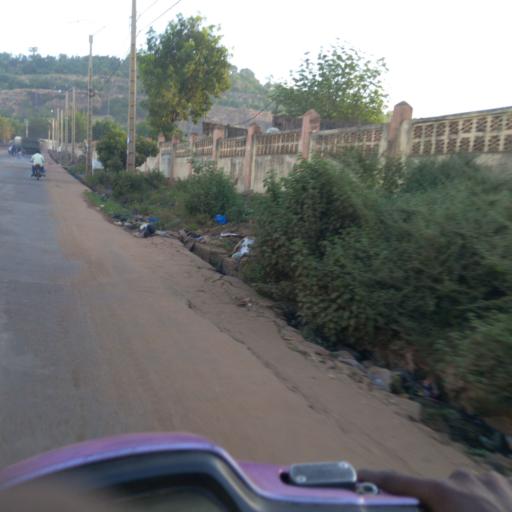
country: ML
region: Bamako
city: Bamako
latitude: 12.6547
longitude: -8.0121
